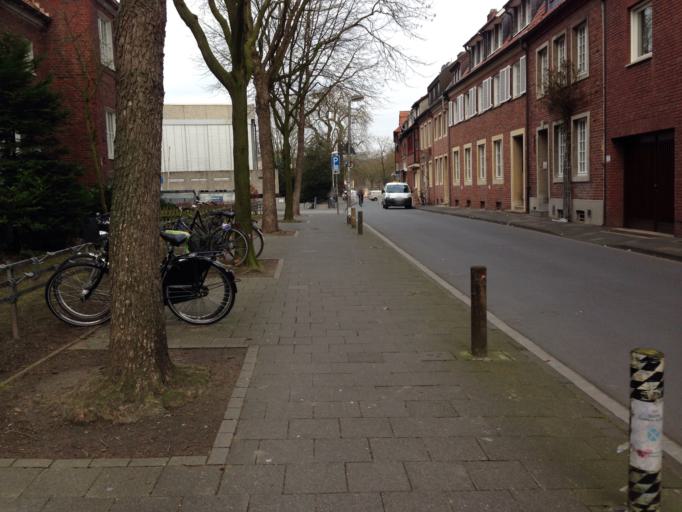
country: DE
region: North Rhine-Westphalia
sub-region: Regierungsbezirk Munster
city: Muenster
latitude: 51.9628
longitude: 7.6194
